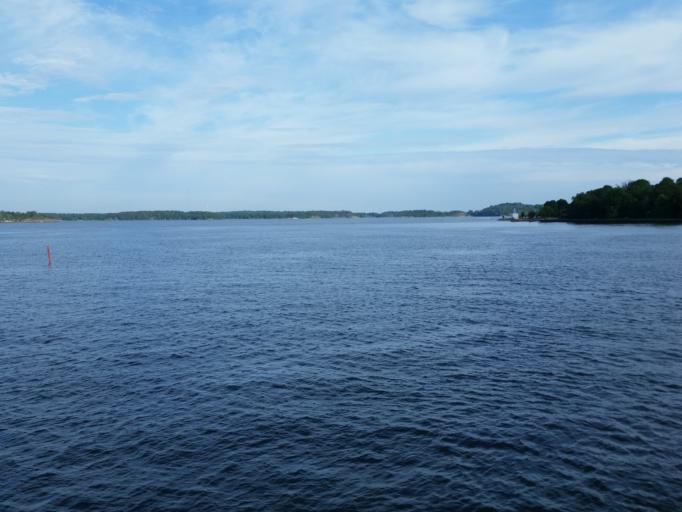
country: FI
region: Uusimaa
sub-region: Helsinki
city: Helsinki
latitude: 60.1523
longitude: 24.9833
